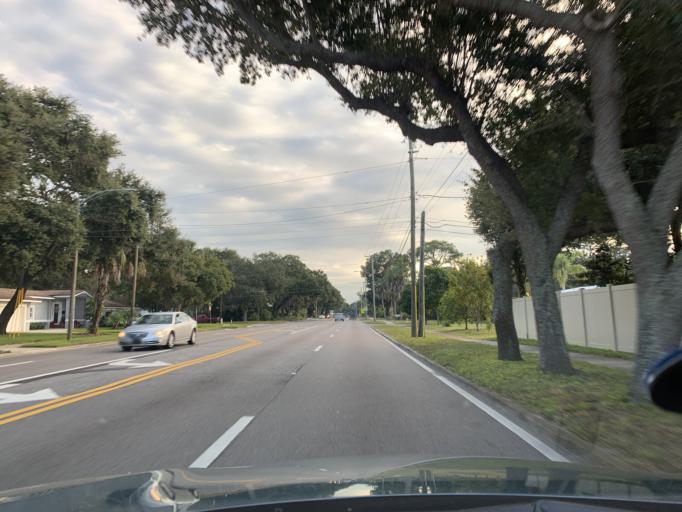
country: US
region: Florida
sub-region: Pinellas County
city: Bay Pines
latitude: 27.7991
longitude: -82.7539
